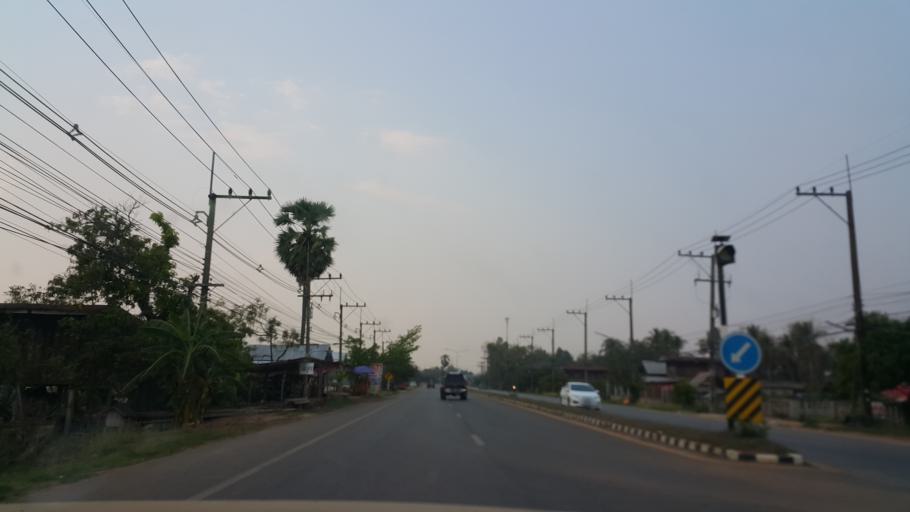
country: TH
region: Nakhon Phanom
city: Renu Nakhon
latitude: 17.0049
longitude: 104.7231
